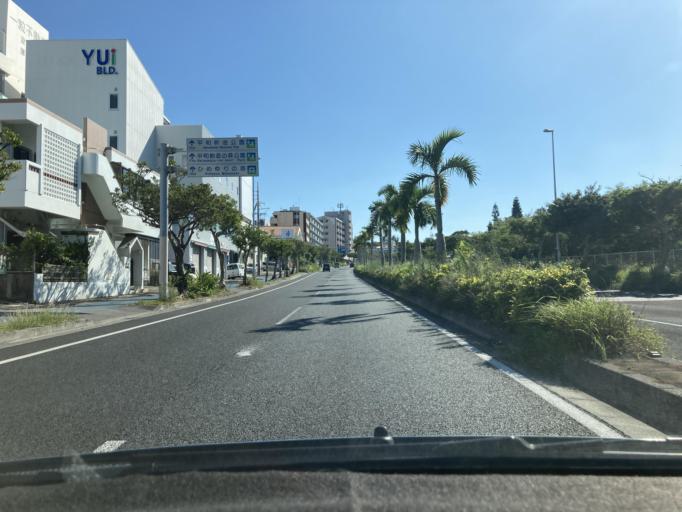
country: JP
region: Okinawa
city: Naha-shi
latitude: 26.2018
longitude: 127.6620
